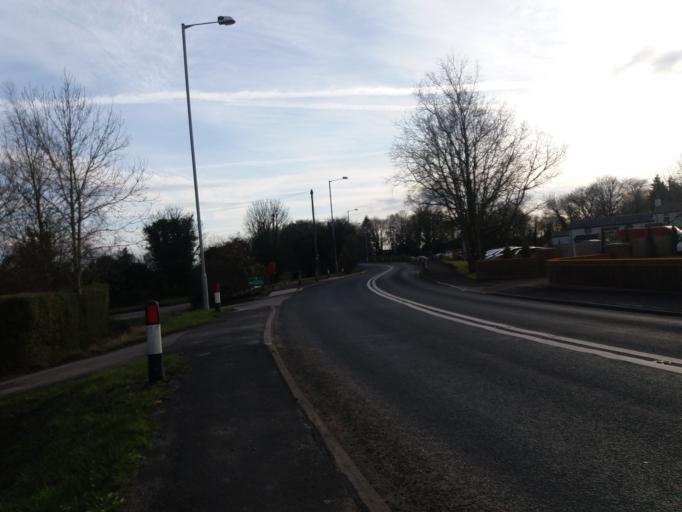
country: GB
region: England
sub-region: Lancashire
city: Euxton
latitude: 53.6461
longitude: -2.6770
